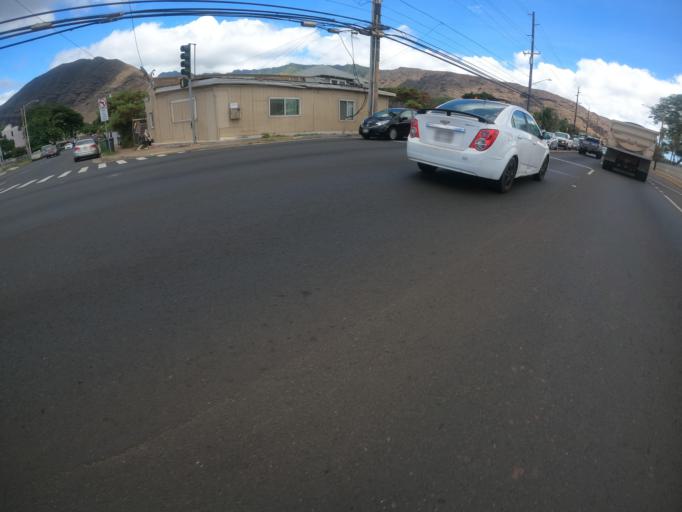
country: US
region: Hawaii
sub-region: Honolulu County
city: Nanakuli
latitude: 21.3844
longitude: -158.1486
